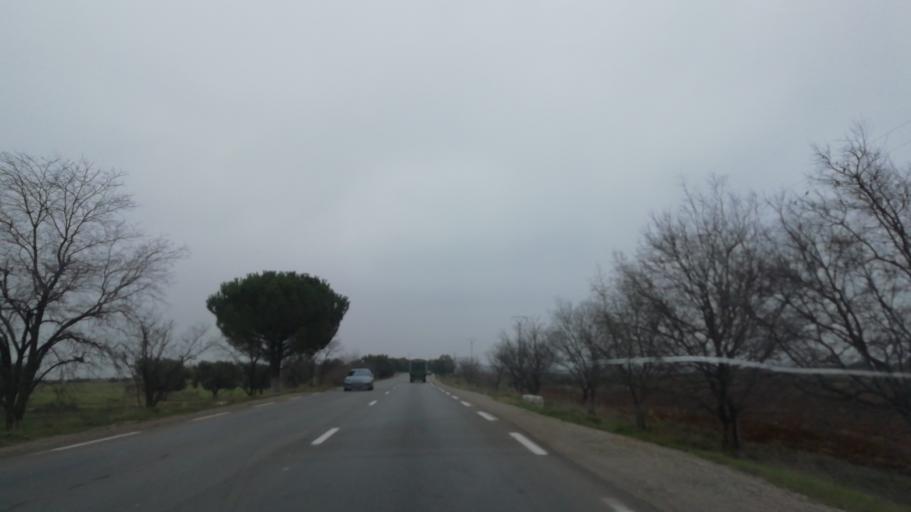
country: DZ
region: Mascara
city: Mascara
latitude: 35.3149
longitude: 0.3816
